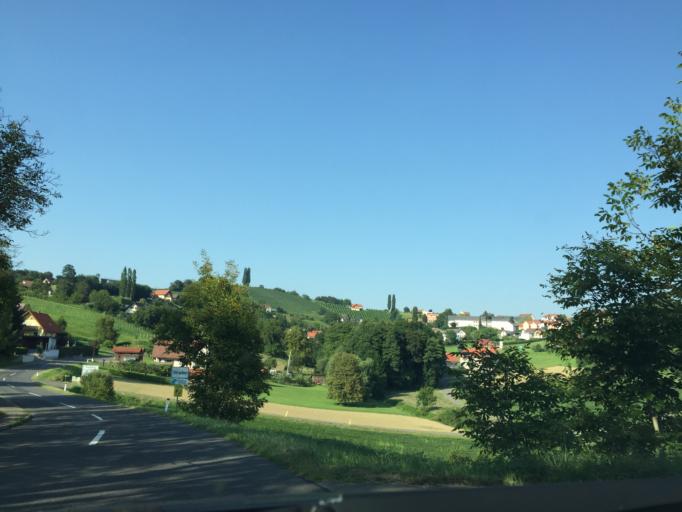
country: AT
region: Styria
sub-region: Politischer Bezirk Suedoststeiermark
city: Straden
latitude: 46.8056
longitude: 15.8612
